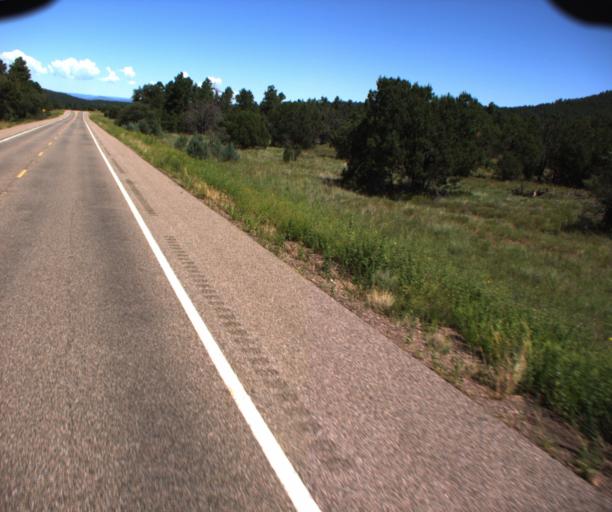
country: US
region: Arizona
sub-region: Gila County
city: San Carlos
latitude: 33.6684
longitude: -110.5724
